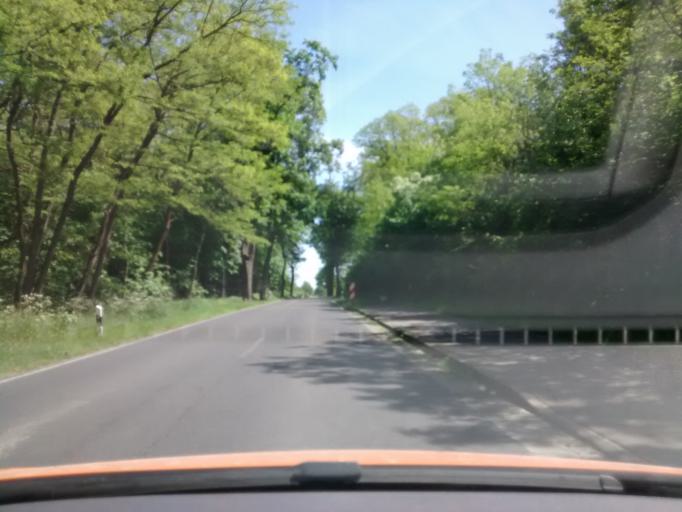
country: DE
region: Brandenburg
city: Reichenwalde
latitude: 52.2644
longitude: 13.9741
